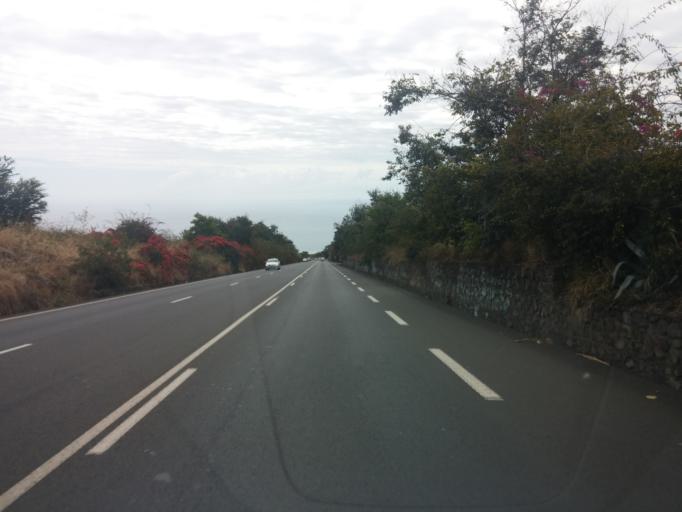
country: RE
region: Reunion
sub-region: Reunion
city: Saint-Paul
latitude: -21.0258
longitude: 55.2740
